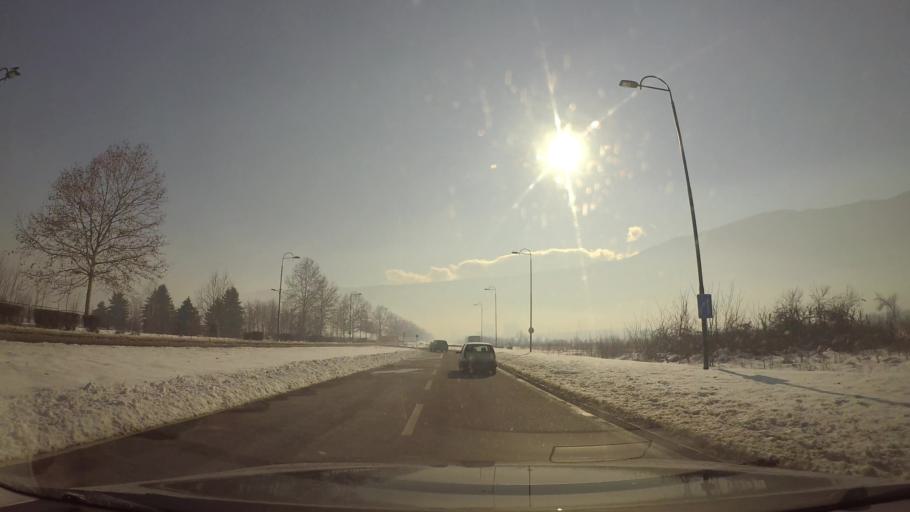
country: BA
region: Federation of Bosnia and Herzegovina
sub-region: Kanton Sarajevo
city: Sarajevo
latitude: 43.8060
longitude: 18.3113
